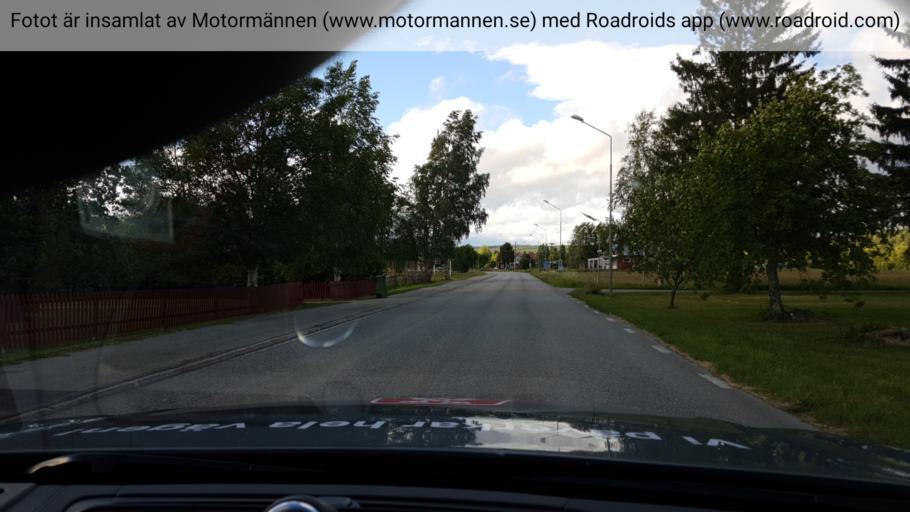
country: SE
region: Jaemtland
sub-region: Harjedalens Kommun
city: Sveg
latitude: 62.4478
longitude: 13.8583
